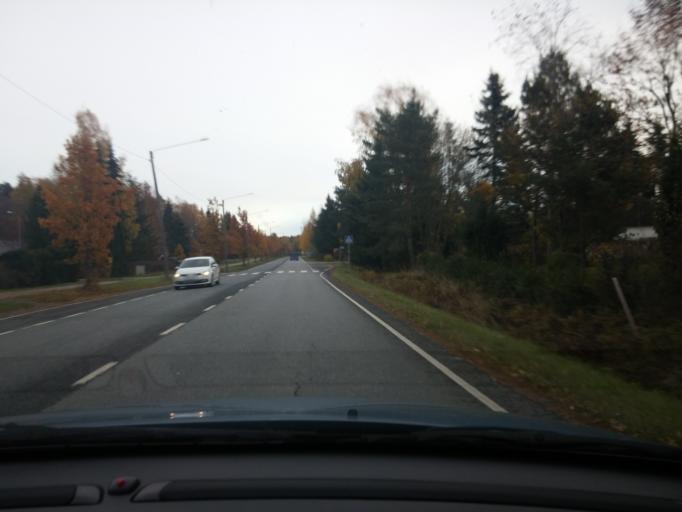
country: FI
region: Haeme
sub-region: Forssa
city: Tammela
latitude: 60.8069
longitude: 23.7876
